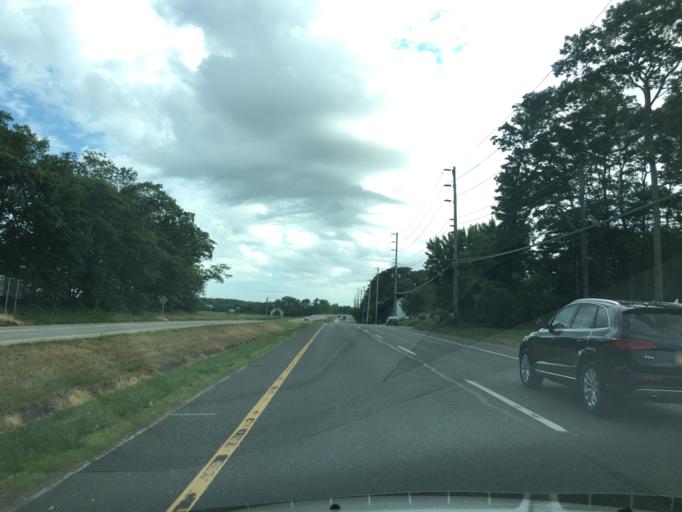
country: US
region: New York
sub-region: Suffolk County
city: Cutchogue
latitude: 41.0293
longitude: -72.4963
